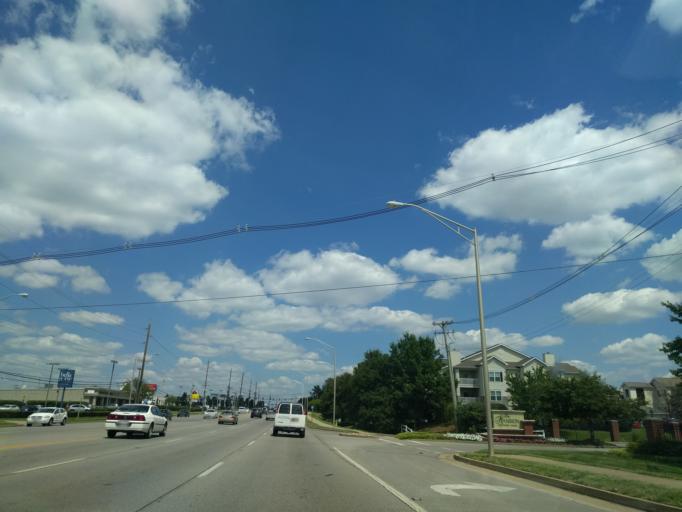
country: US
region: Kentucky
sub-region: Fayette County
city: Monticello
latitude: 37.9818
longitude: -84.5278
